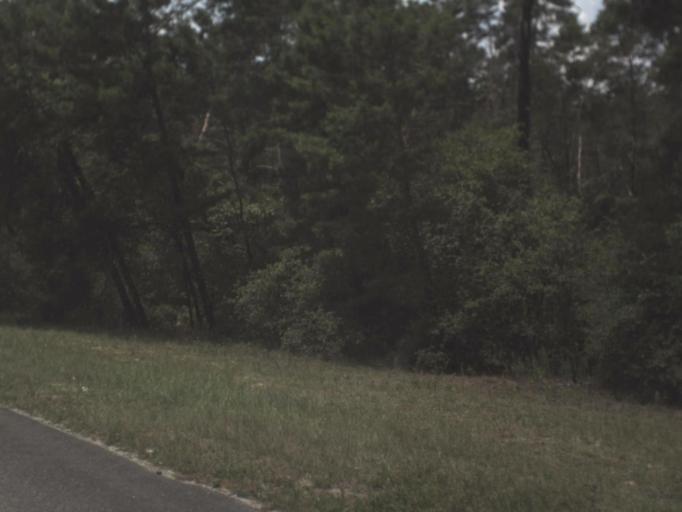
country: US
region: Florida
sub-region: Putnam County
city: Crescent City
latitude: 29.3954
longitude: -81.7366
